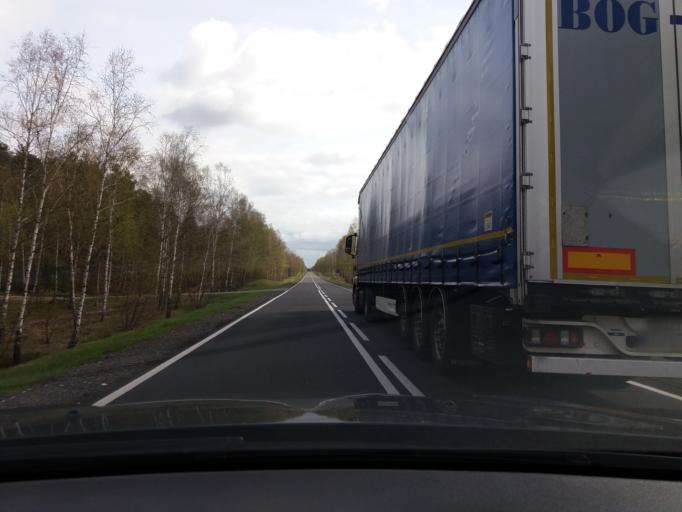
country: PL
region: Lubusz
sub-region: Powiat miedzyrzecki
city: Bledzew
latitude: 52.5912
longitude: 15.3701
